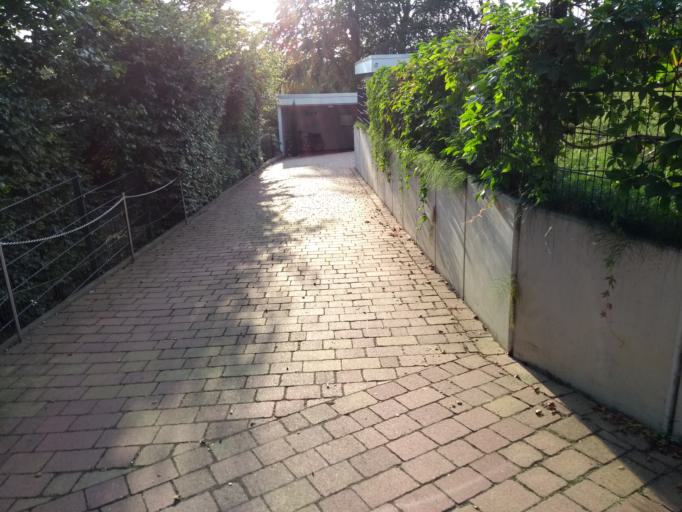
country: DE
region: Mecklenburg-Vorpommern
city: Ostseebad Sellin
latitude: 54.3762
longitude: 13.7030
